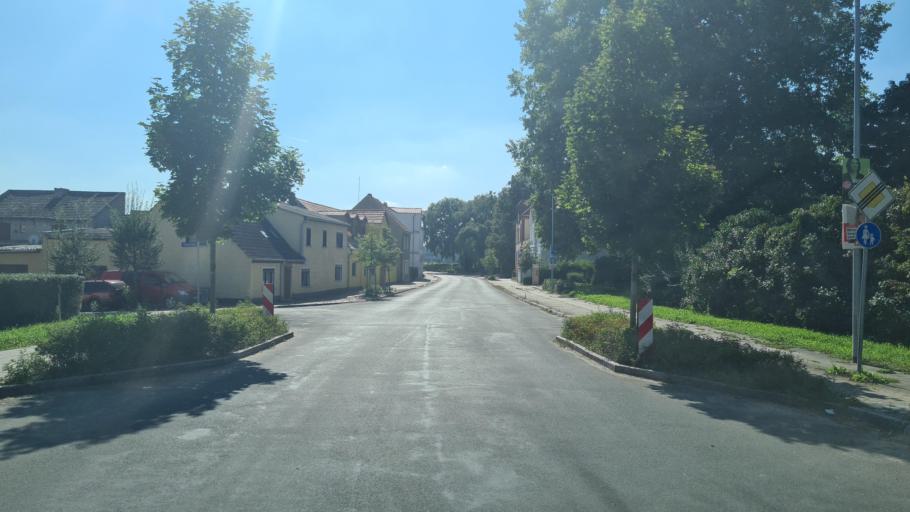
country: DE
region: Brandenburg
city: Friesack
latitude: 52.7437
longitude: 12.5800
